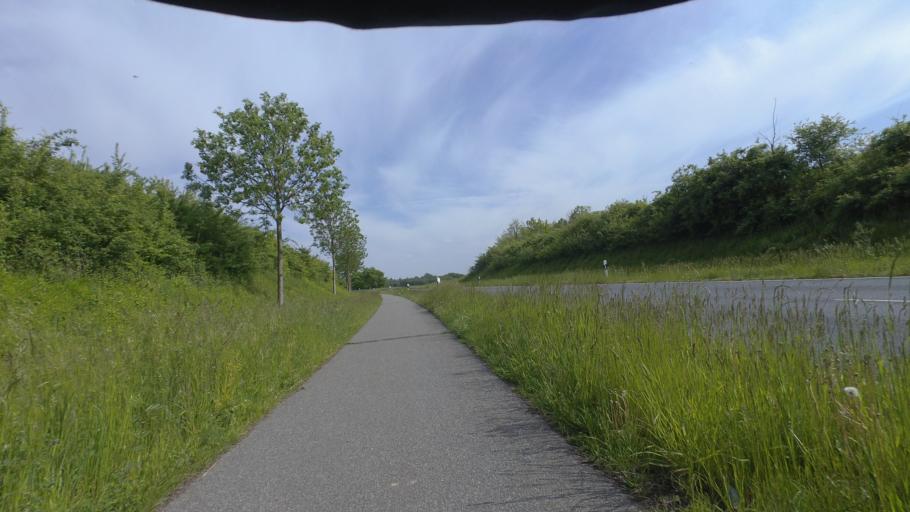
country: DE
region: Saxony-Anhalt
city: Hotensleben
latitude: 52.1237
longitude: 11.0012
